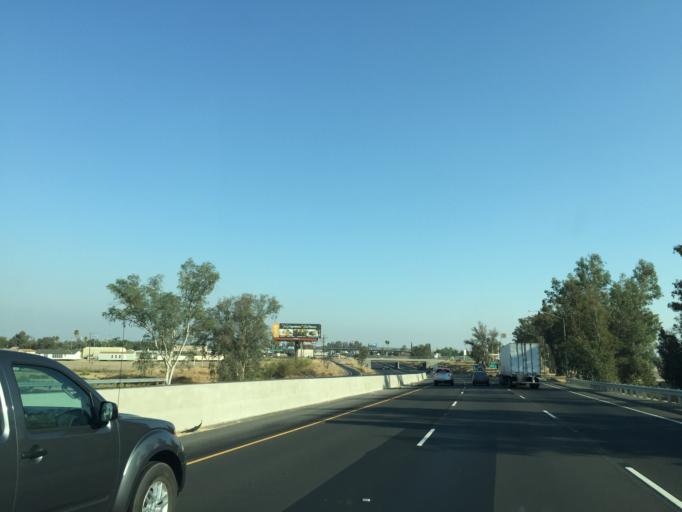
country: US
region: California
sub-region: Tulare County
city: Goshen
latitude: 36.3541
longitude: -119.4282
